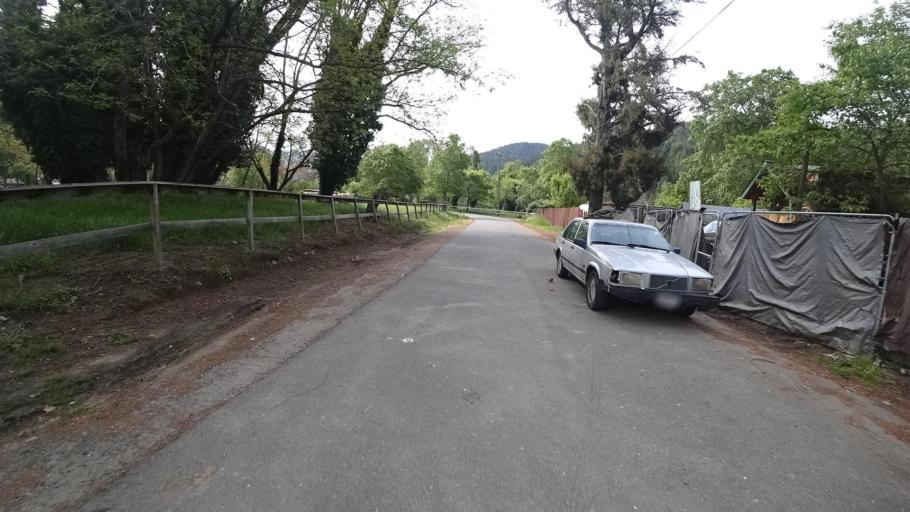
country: US
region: California
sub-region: Humboldt County
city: Redway
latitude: 40.2081
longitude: -123.7896
